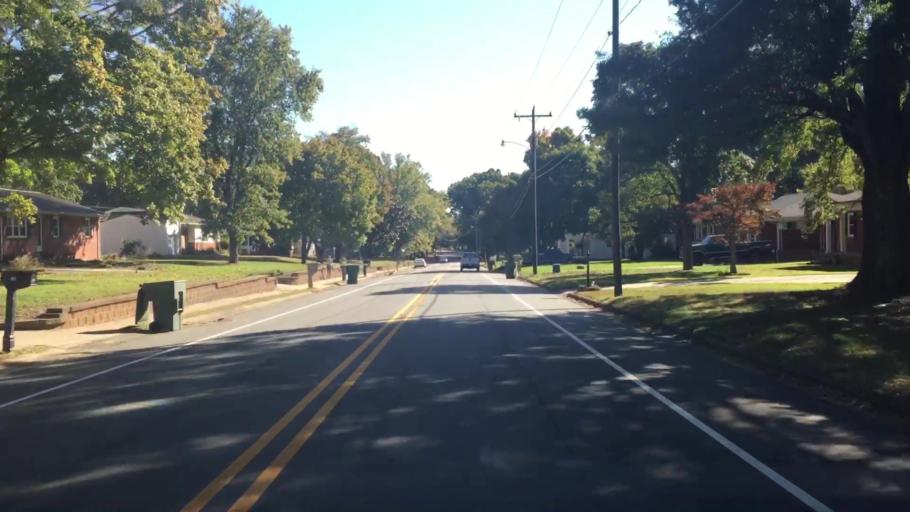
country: US
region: North Carolina
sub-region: Iredell County
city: Mooresville
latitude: 35.5731
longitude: -80.8013
